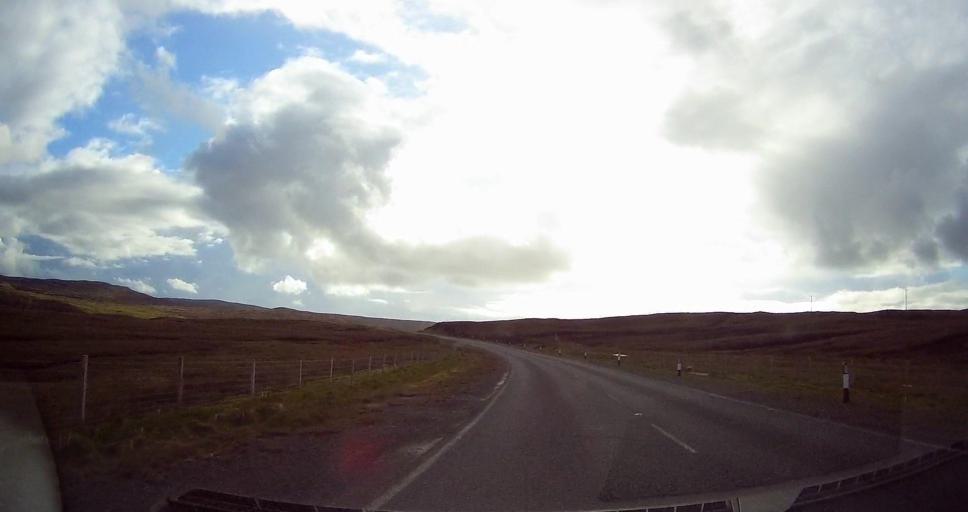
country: GB
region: Scotland
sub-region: Shetland Islands
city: Lerwick
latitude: 60.3495
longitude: -1.2156
